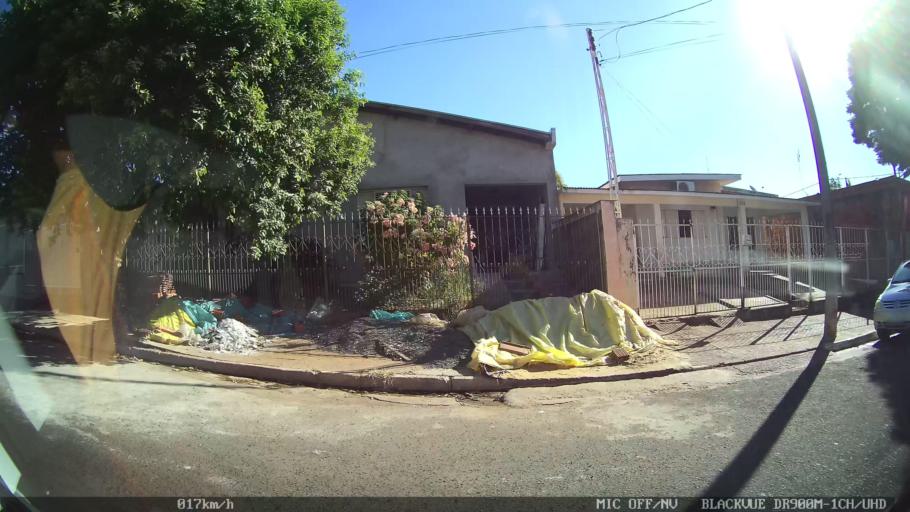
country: BR
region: Sao Paulo
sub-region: Olimpia
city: Olimpia
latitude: -20.7475
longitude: -48.9092
